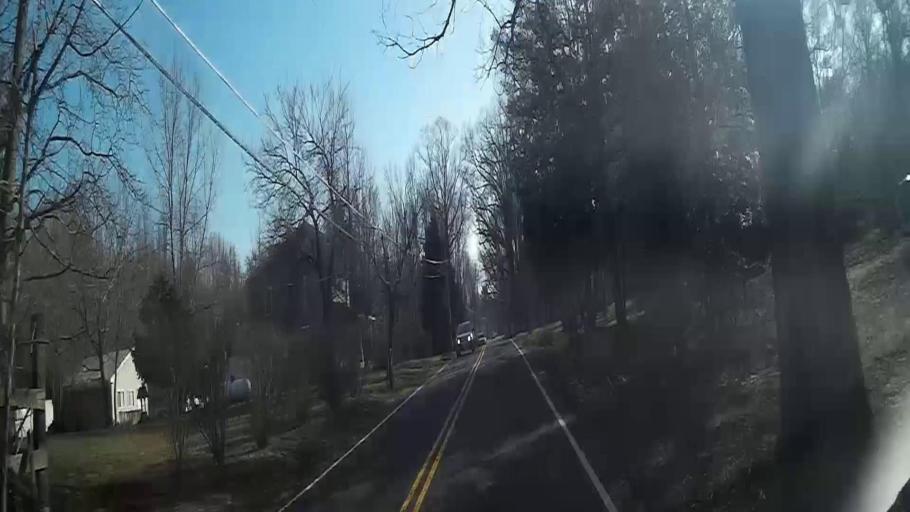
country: US
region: New Jersey
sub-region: Burlington County
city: Marlton
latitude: 39.8559
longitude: -74.9064
